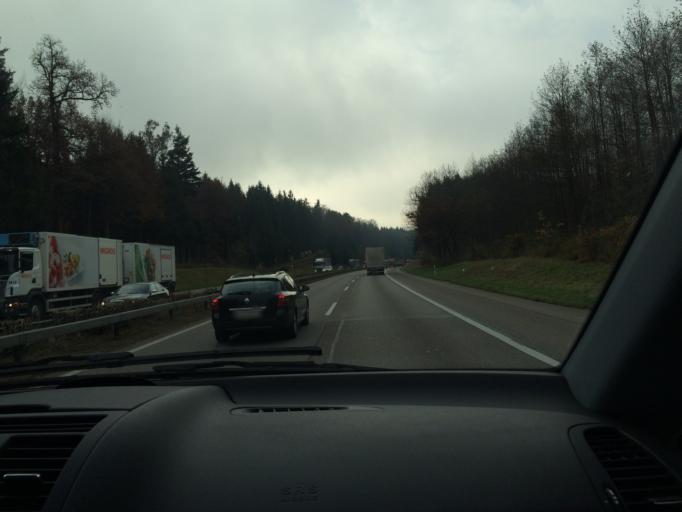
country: CH
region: Bern
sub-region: Emmental District
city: Hindelbank
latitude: 47.0354
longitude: 7.5285
